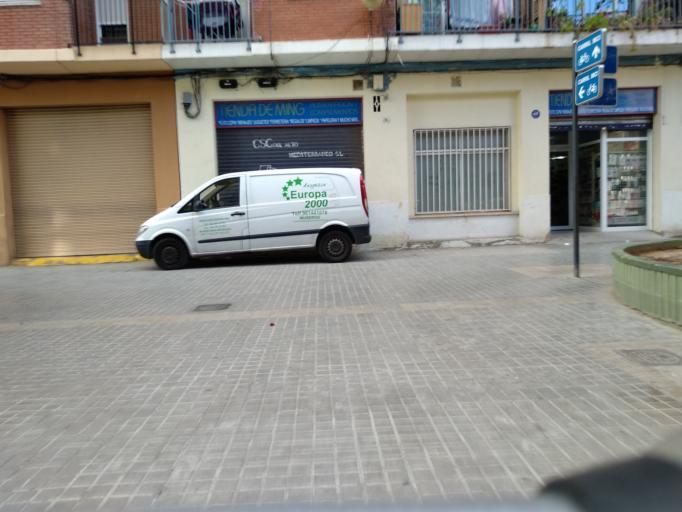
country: ES
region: Valencia
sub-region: Provincia de Valencia
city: Tavernes Blanques
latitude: 39.4916
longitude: -0.3704
